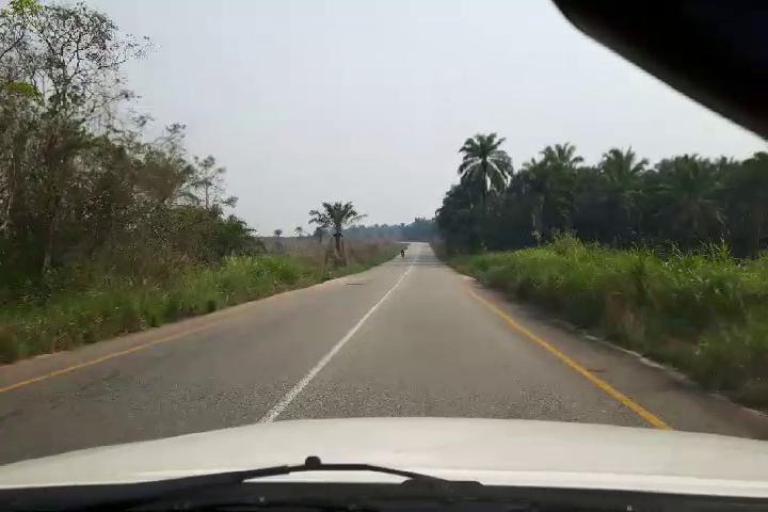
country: SL
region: Southern Province
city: Largo
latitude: 8.2172
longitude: -12.0747
